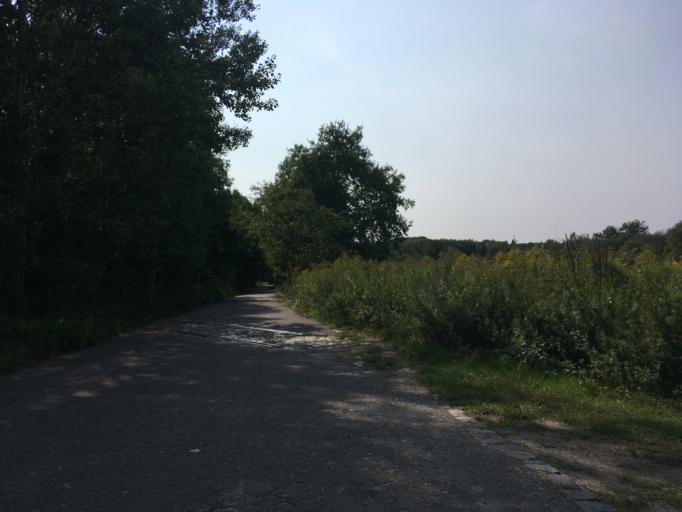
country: DE
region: Berlin
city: Konradshohe
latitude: 52.6004
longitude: 13.1970
